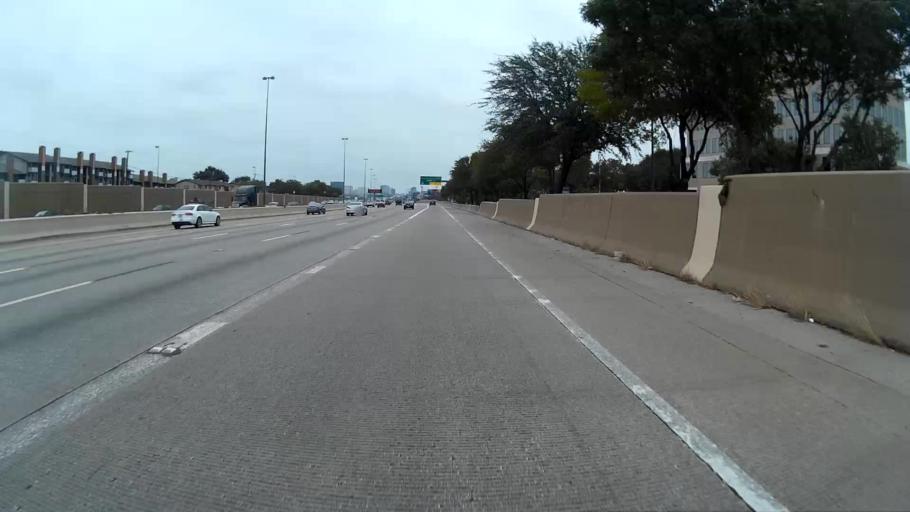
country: US
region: Texas
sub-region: Dallas County
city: University Park
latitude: 32.8916
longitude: -96.7691
